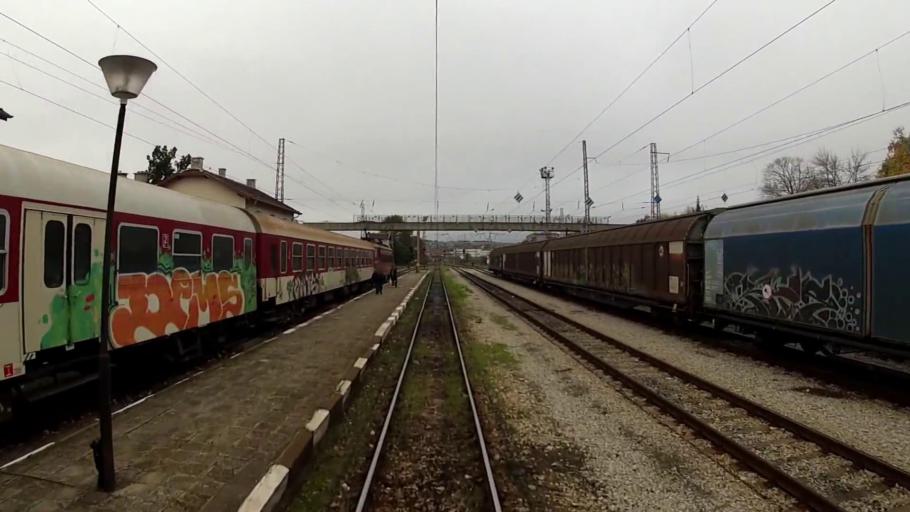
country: BG
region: Sofiya
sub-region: Obshtina Dragoman
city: Dragoman
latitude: 42.9235
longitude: 22.9327
